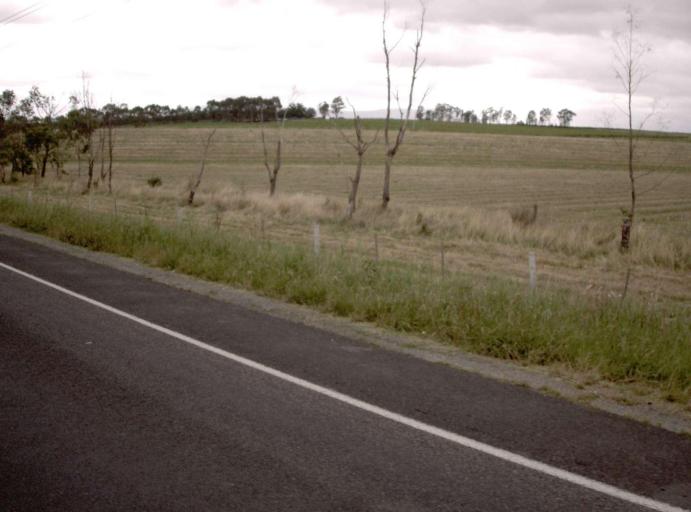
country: AU
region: Victoria
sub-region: Yarra Ranges
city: Yarra Glen
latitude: -37.6837
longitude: 145.3776
